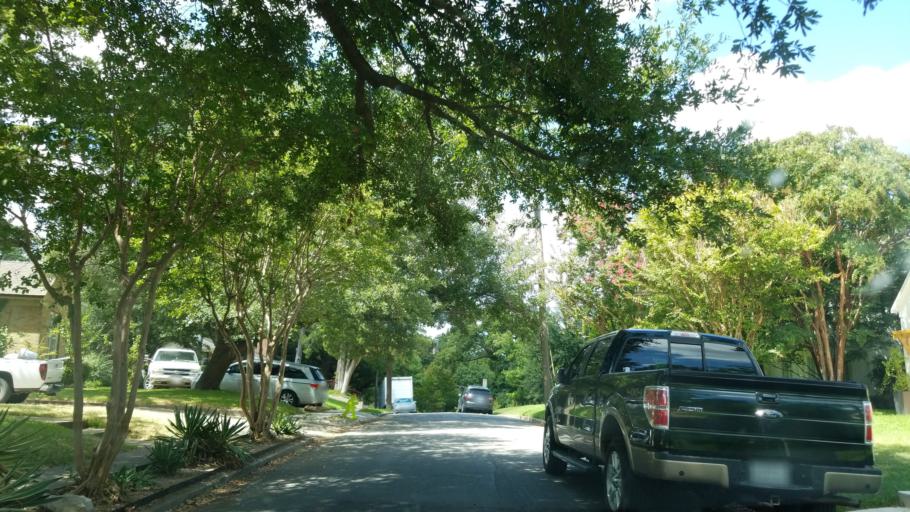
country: US
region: Texas
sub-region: Dallas County
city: Dallas
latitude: 32.7603
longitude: -96.8286
